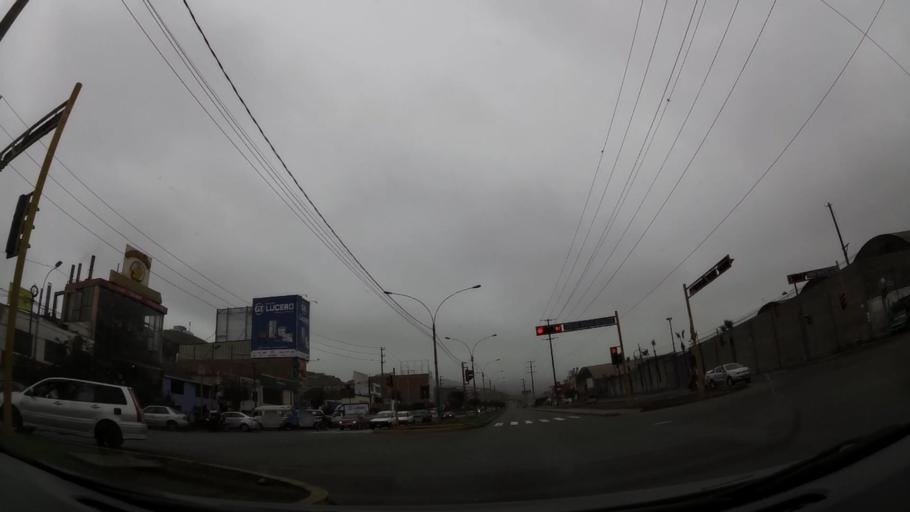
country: PE
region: Lima
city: Ventanilla
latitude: -11.8716
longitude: -77.1275
